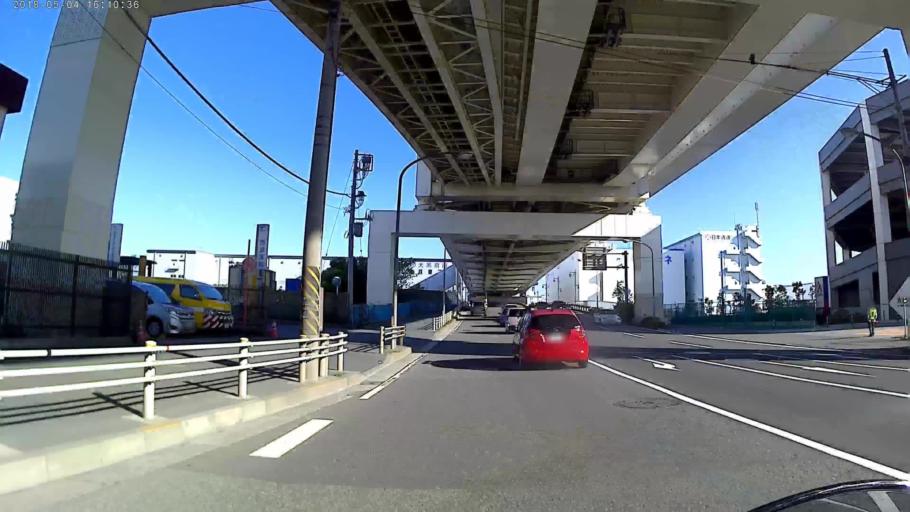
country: JP
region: Kanagawa
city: Yokohama
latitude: 35.4907
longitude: 139.6715
